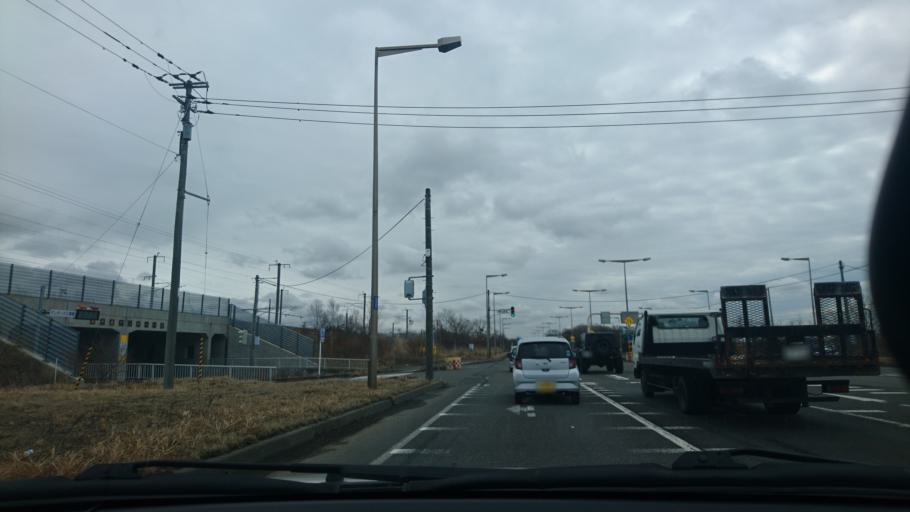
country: JP
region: Hokkaido
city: Chitose
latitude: 42.7962
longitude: 141.6890
